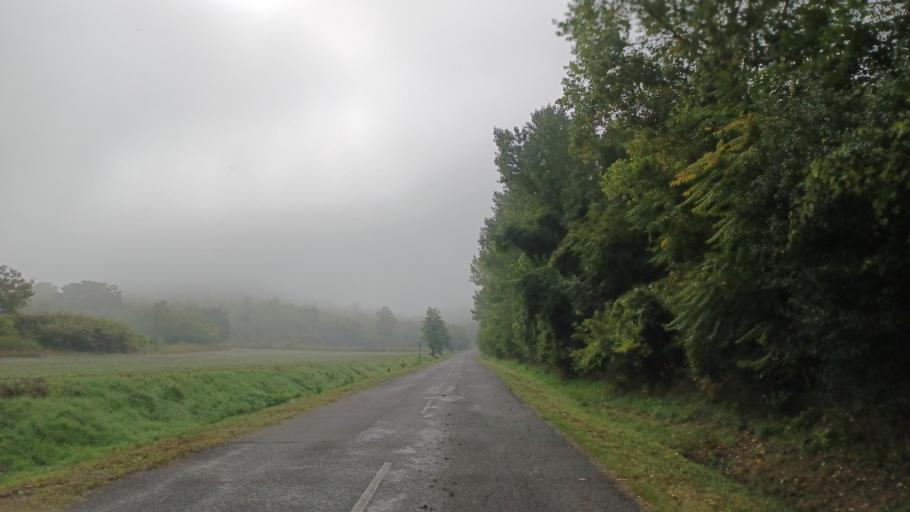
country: HU
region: Tolna
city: Pincehely
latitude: 46.6858
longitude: 18.4614
